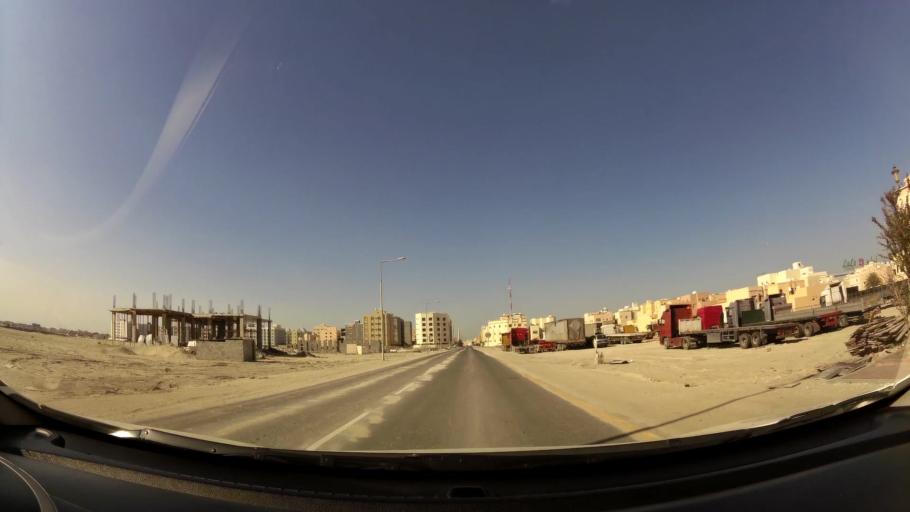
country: BH
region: Muharraq
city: Al Hadd
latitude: 26.2363
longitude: 50.6481
